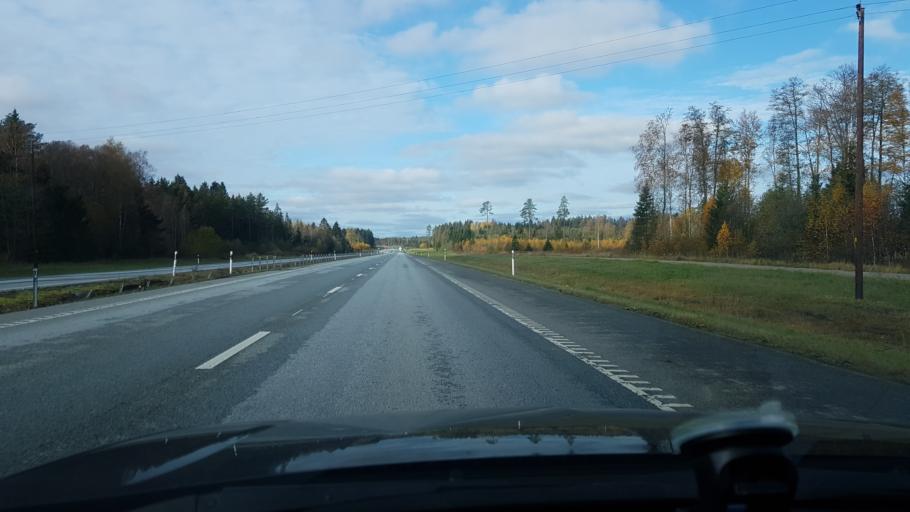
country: EE
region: Laeaene-Virumaa
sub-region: Kadrina vald
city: Kadrina
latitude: 59.4546
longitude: 26.0524
